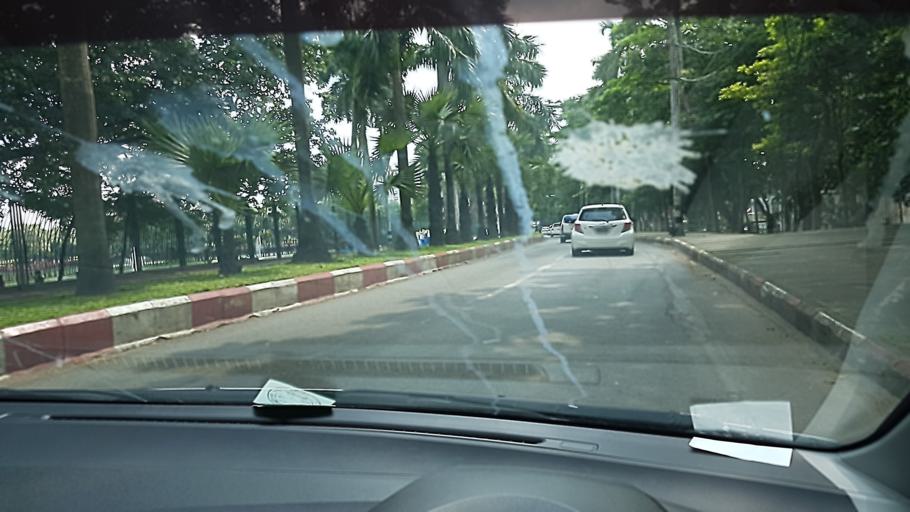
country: MM
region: Yangon
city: Yangon
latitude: 16.7926
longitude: 96.1673
